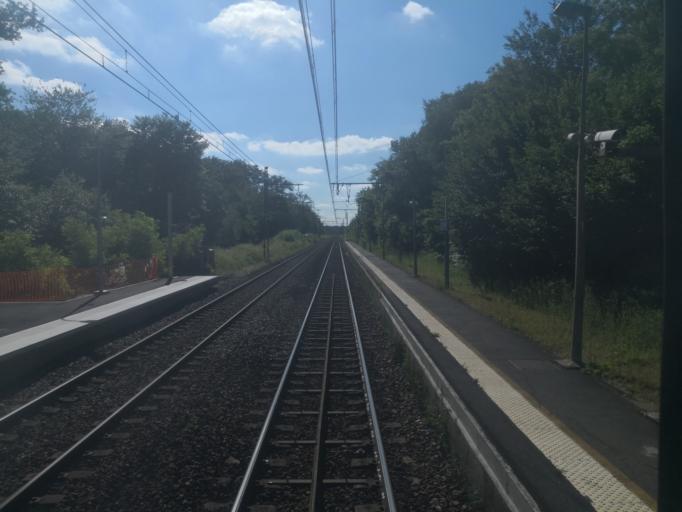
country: FR
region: Ile-de-France
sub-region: Departement de Seine-et-Marne
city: Thomery
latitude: 48.3944
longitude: 2.7624
